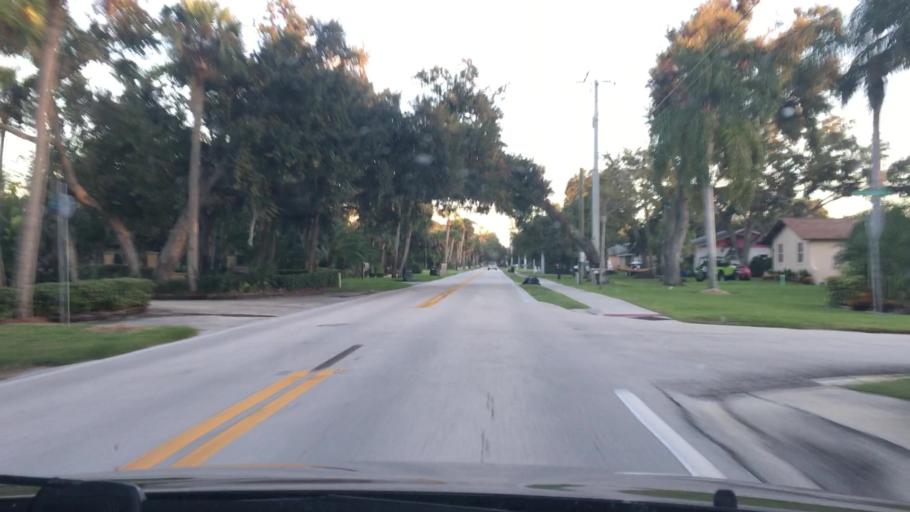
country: US
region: Florida
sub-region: Volusia County
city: Ormond Beach
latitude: 29.3054
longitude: -81.0653
